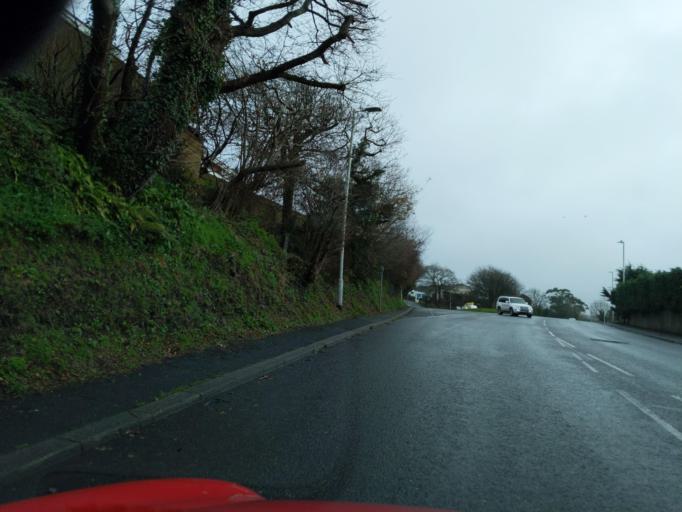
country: GB
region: England
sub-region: Devon
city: Plympton
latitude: 50.3838
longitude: -4.0350
